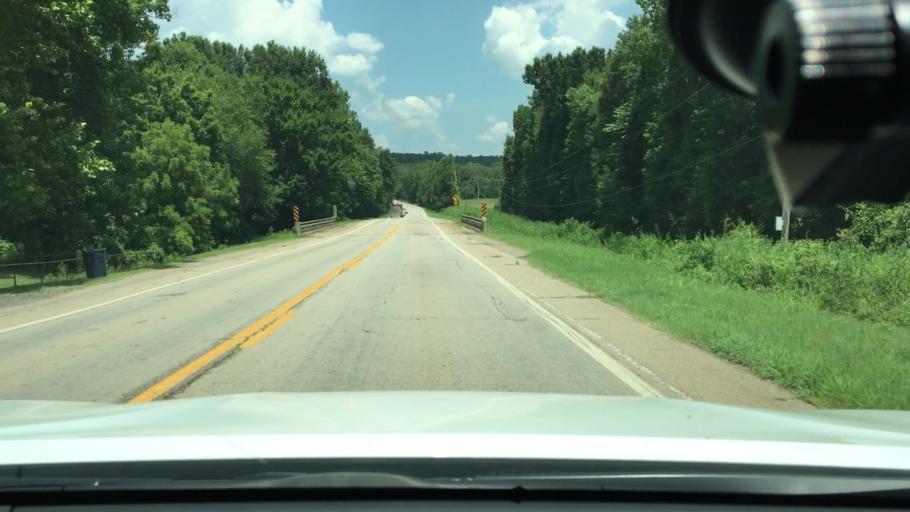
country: US
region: Arkansas
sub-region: Logan County
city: Booneville
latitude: 35.2043
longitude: -93.9243
